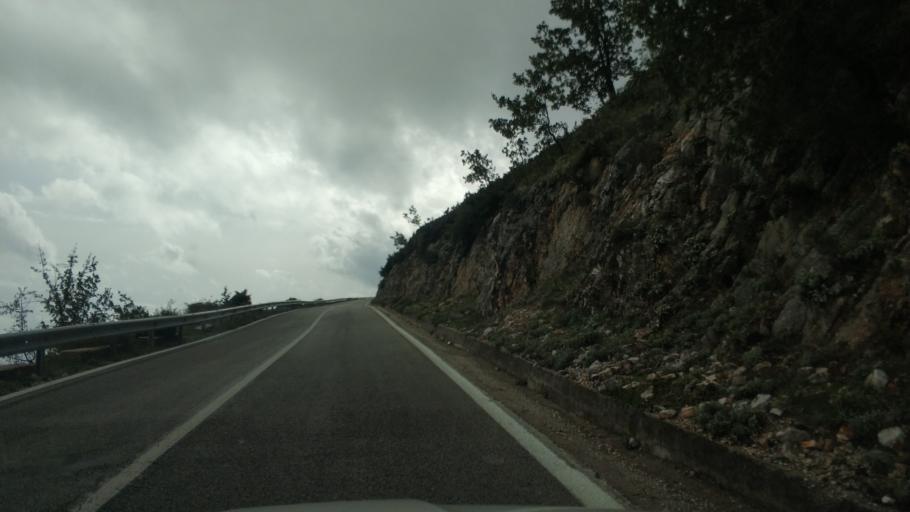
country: AL
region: Vlore
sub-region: Rrethi i Vlores
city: Vranisht
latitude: 40.1855
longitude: 19.6054
